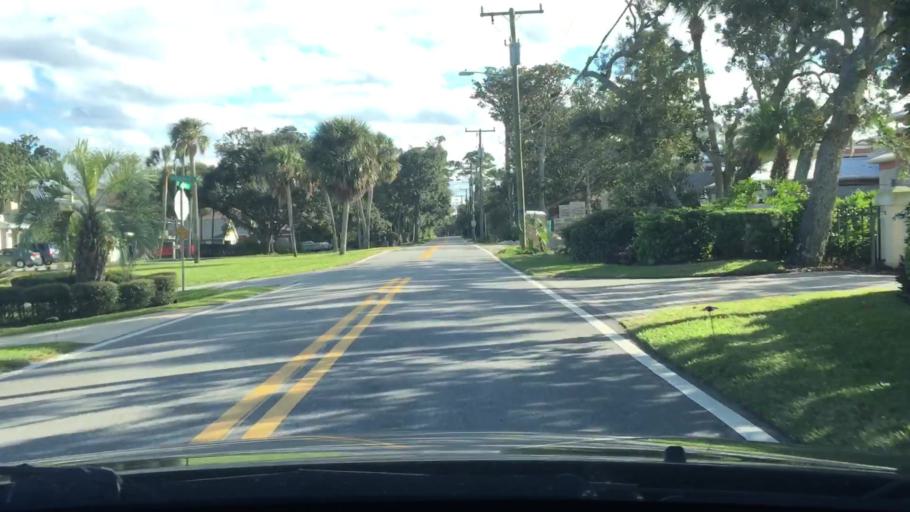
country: US
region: Florida
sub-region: Volusia County
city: Ormond Beach
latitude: 29.3112
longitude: -81.0578
